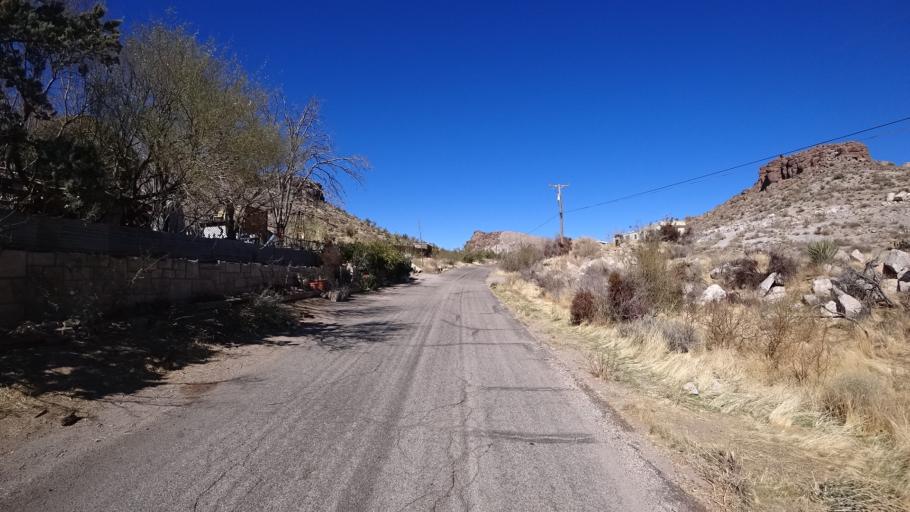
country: US
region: Arizona
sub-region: Mohave County
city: Kingman
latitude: 35.2017
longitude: -114.0612
